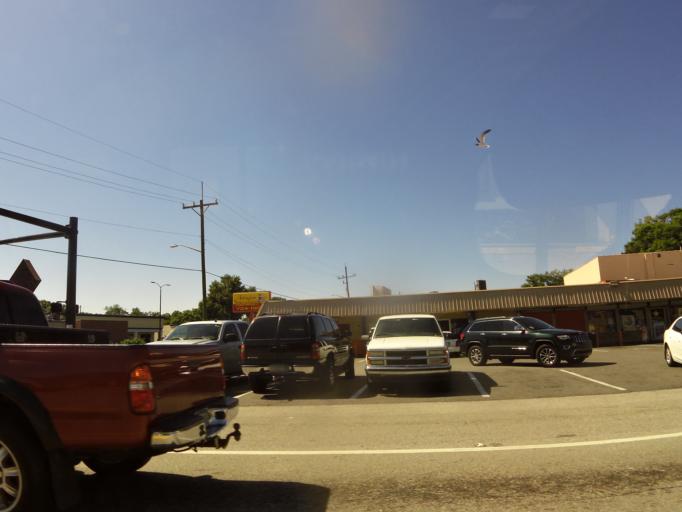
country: US
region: Florida
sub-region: Duval County
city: Jacksonville
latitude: 30.3310
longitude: -81.5876
